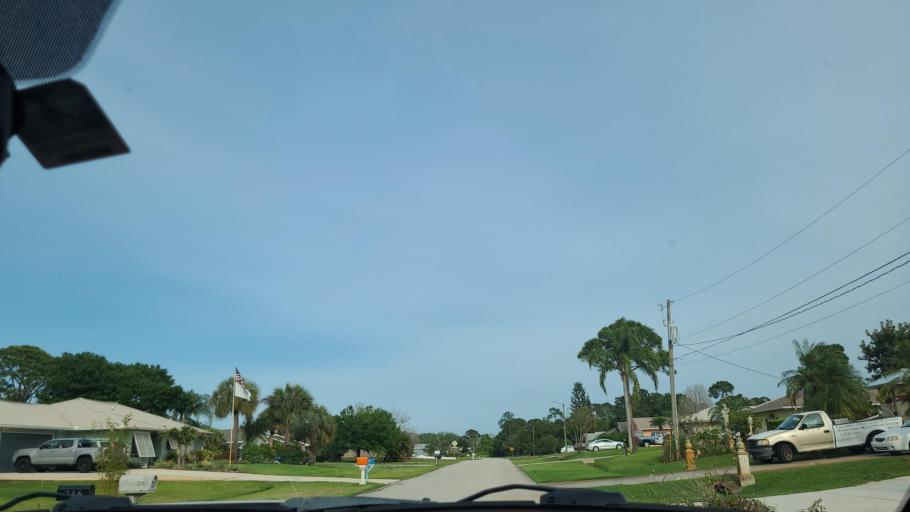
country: US
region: Florida
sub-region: Indian River County
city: Sebastian
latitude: 27.7933
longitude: -80.4753
